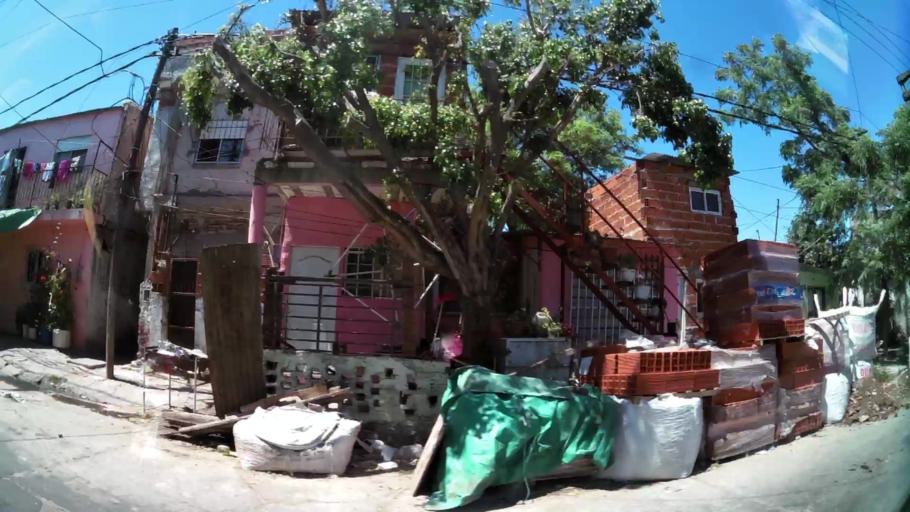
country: AR
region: Buenos Aires
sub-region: Partido de San Isidro
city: San Isidro
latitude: -34.4602
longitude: -58.5429
